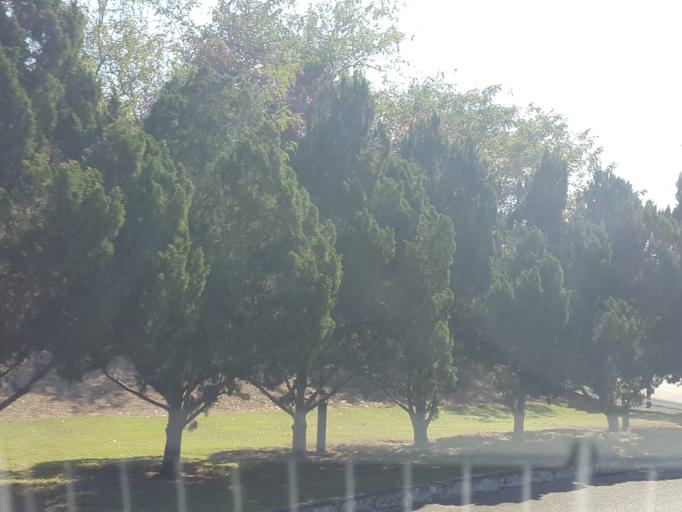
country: TH
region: Chiang Mai
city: Mae Taeng
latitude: 19.0263
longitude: 98.9897
